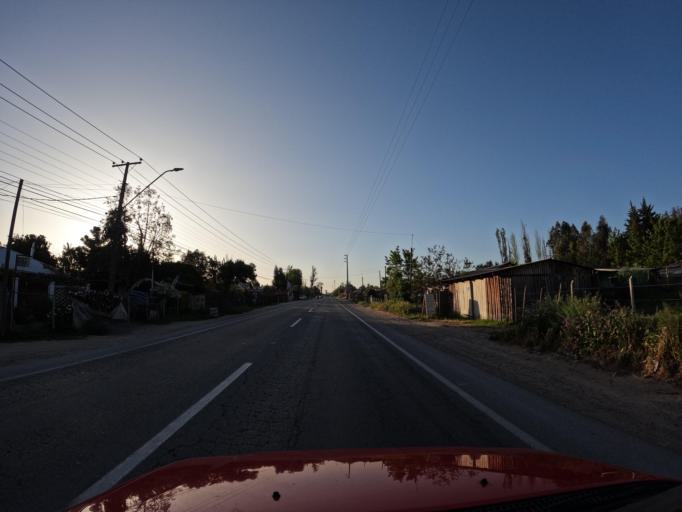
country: CL
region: O'Higgins
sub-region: Provincia de Cachapoal
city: San Vicente
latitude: -34.2643
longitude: -71.3740
